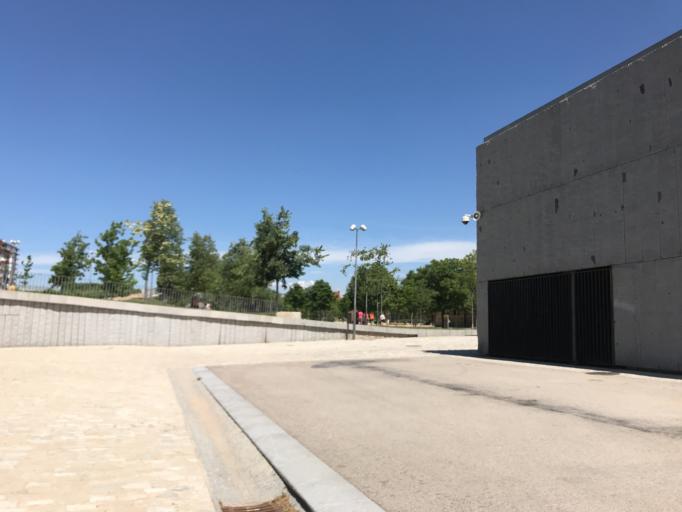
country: ES
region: Madrid
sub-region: Provincia de Madrid
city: Usera
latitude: 40.3918
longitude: -3.6998
